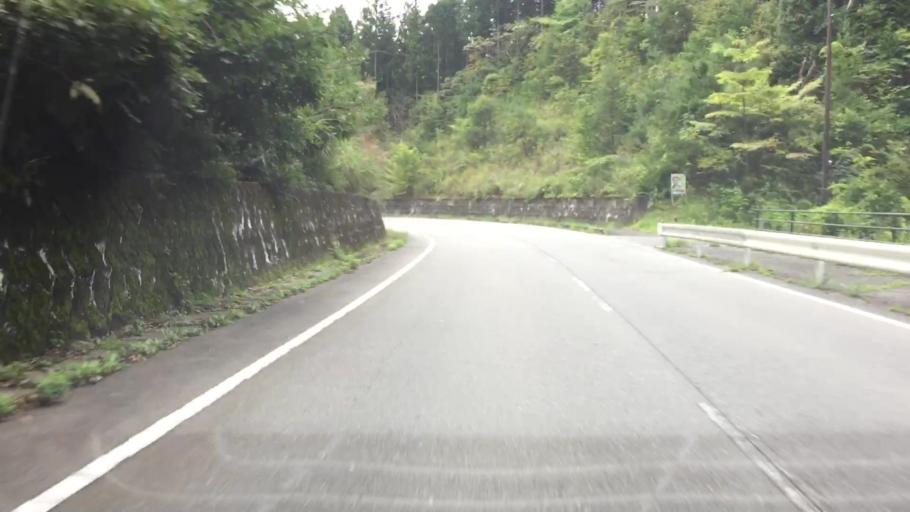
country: JP
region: Tochigi
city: Imaichi
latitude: 36.7487
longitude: 139.6847
